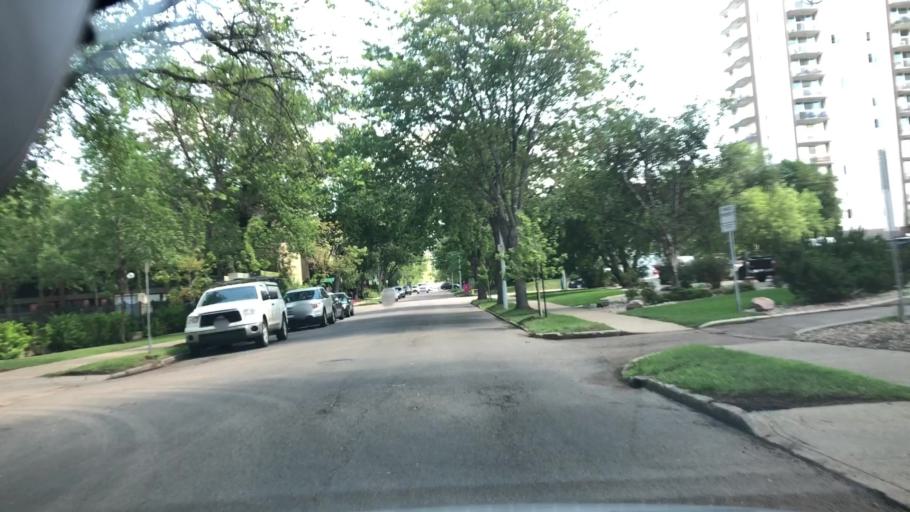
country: CA
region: Alberta
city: Edmonton
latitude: 53.5373
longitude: -113.5170
